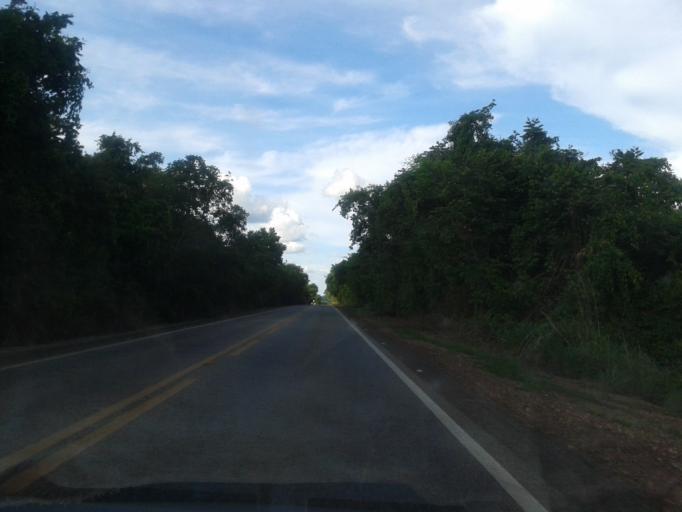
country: BR
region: Goias
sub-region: Mozarlandia
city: Mozarlandia
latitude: -14.5972
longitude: -50.5104
